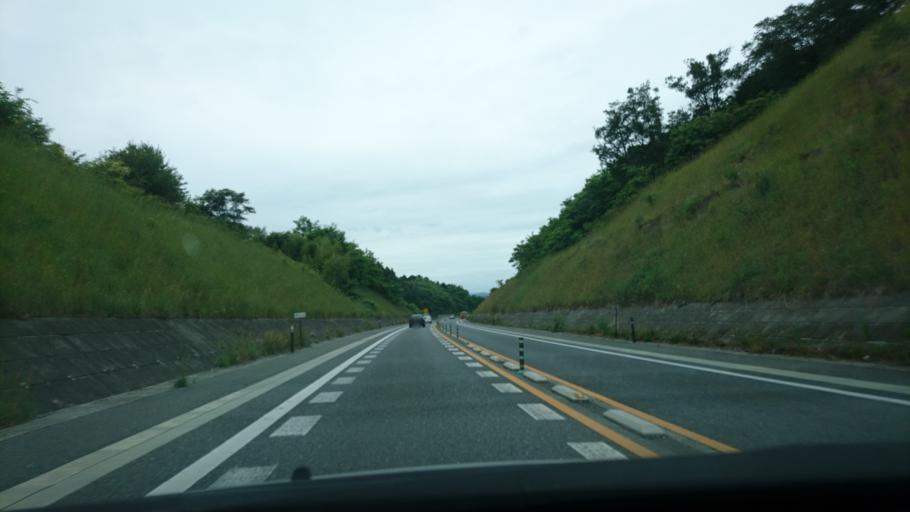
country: JP
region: Miyagi
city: Wakuya
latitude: 38.6397
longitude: 141.2655
